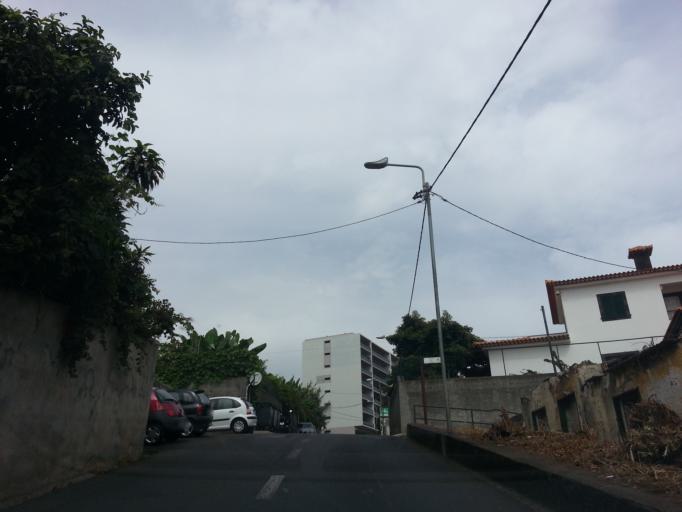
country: PT
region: Madeira
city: Camara de Lobos
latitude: 32.6449
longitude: -16.9422
